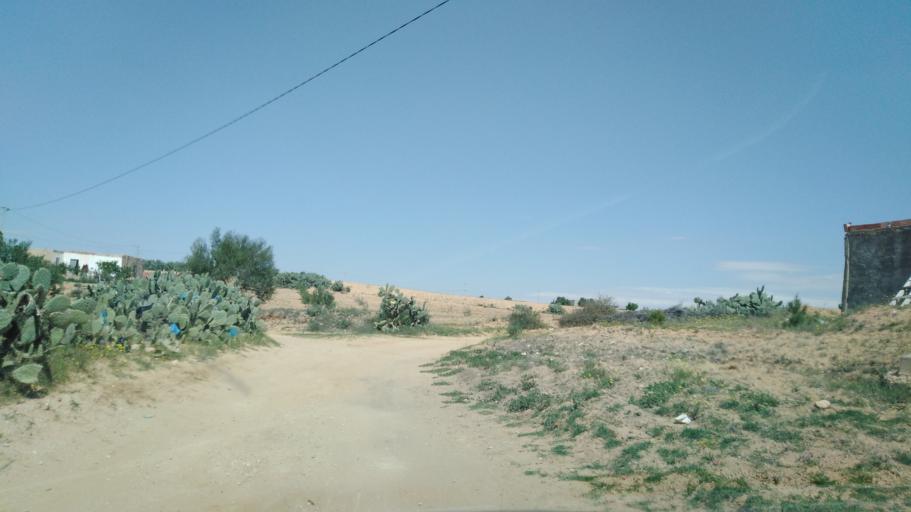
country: TN
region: Safaqis
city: Sfax
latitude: 34.7754
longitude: 10.5267
